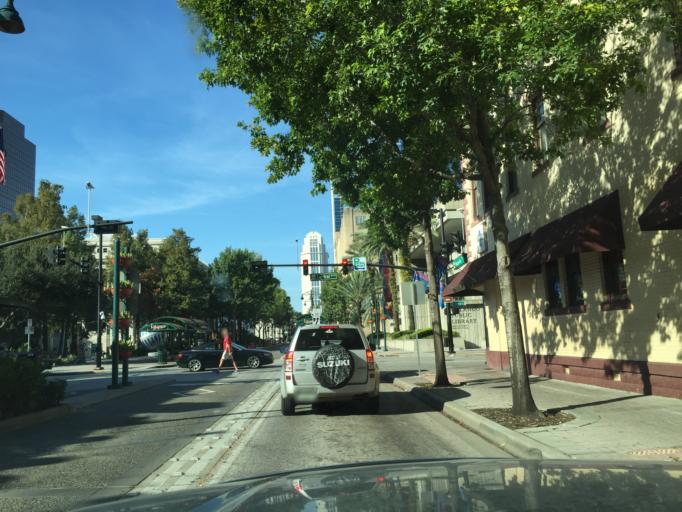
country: US
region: Florida
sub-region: Orange County
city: Orlando
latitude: 28.5421
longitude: -81.3774
